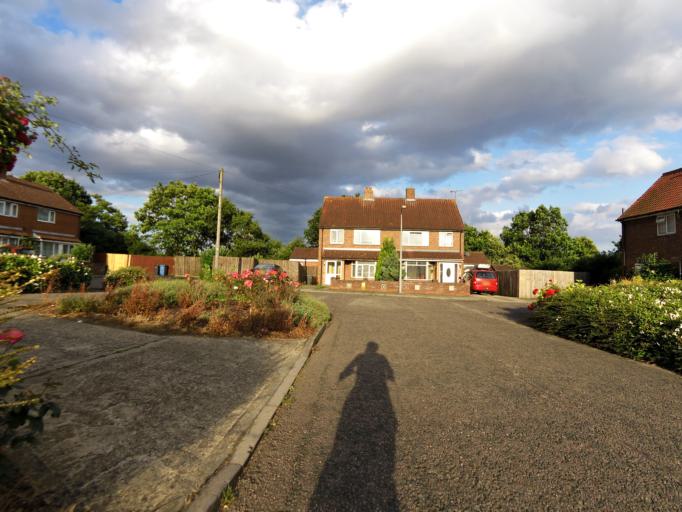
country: GB
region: England
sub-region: Suffolk
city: Bramford
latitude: 52.0765
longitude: 1.1206
